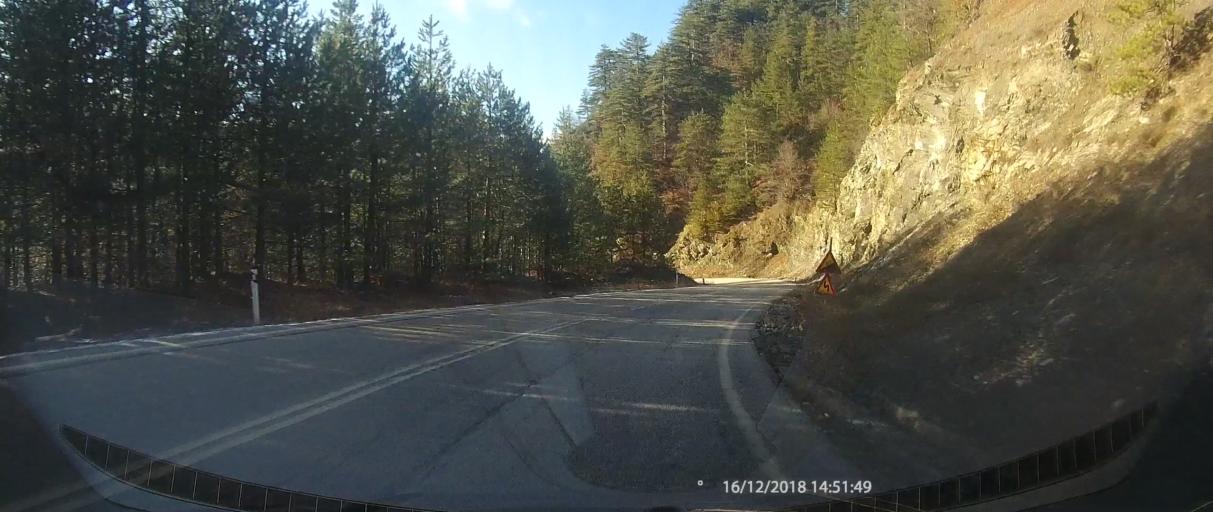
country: GR
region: West Macedonia
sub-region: Nomos Kastorias
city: Nestorio
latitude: 40.2043
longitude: 21.0685
